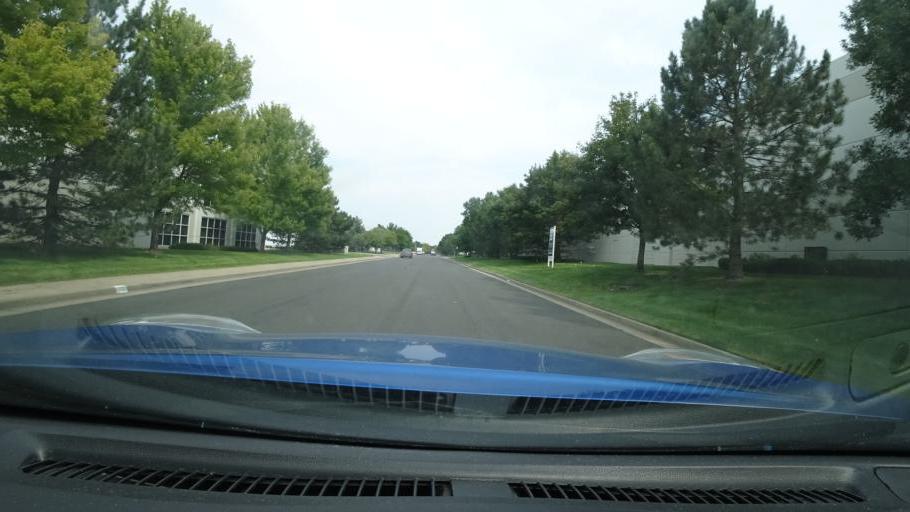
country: US
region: Colorado
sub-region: Adams County
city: Aurora
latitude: 39.7596
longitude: -104.7802
